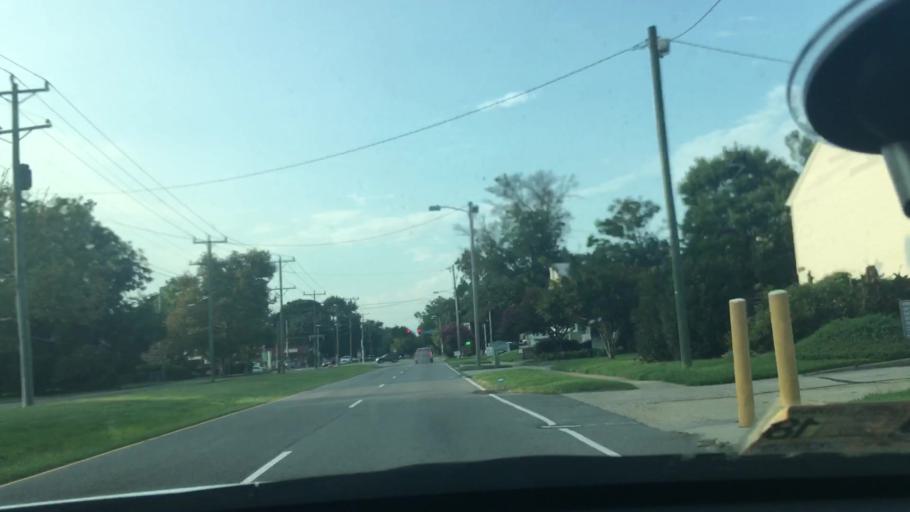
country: US
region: Virginia
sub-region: City of Norfolk
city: Norfolk
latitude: 36.9322
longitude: -76.2441
